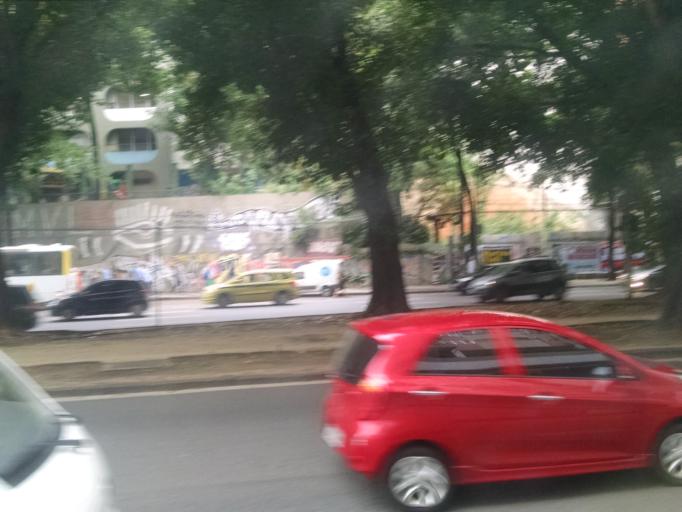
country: BR
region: Rio de Janeiro
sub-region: Rio De Janeiro
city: Rio de Janeiro
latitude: -22.9589
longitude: -43.2004
